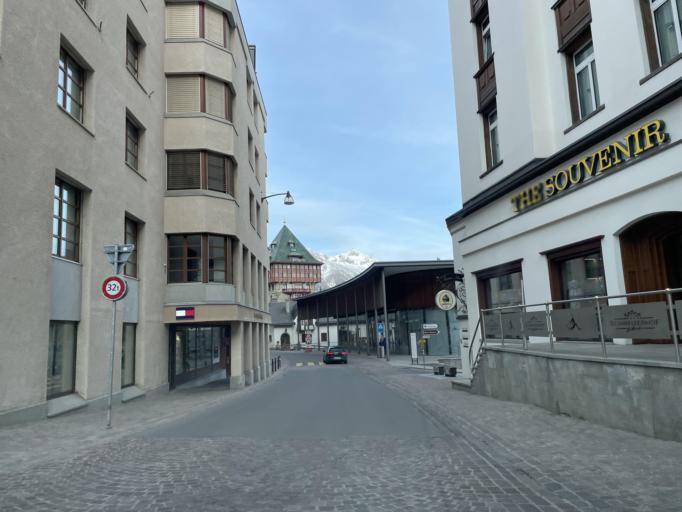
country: CH
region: Grisons
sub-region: Maloja District
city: Saint Moritz
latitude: 46.4971
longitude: 9.8380
